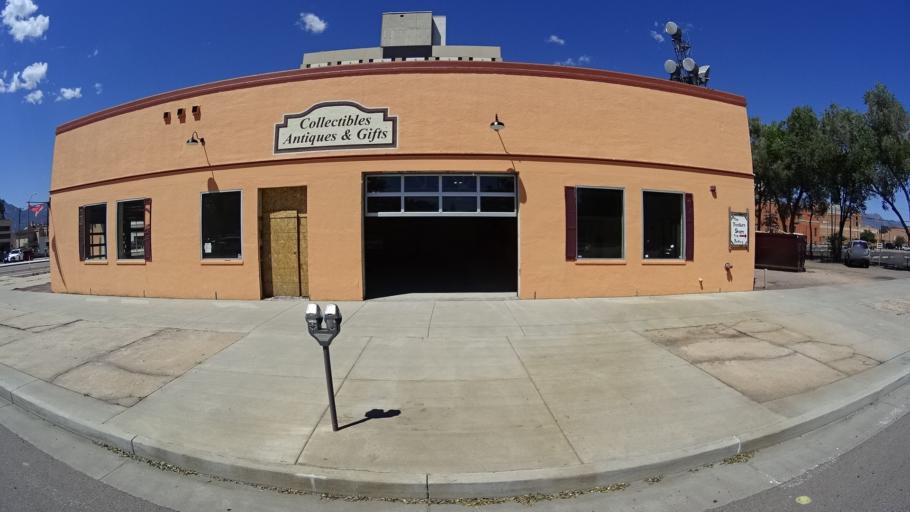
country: US
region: Colorado
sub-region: El Paso County
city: Colorado Springs
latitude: 38.8342
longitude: -104.8181
